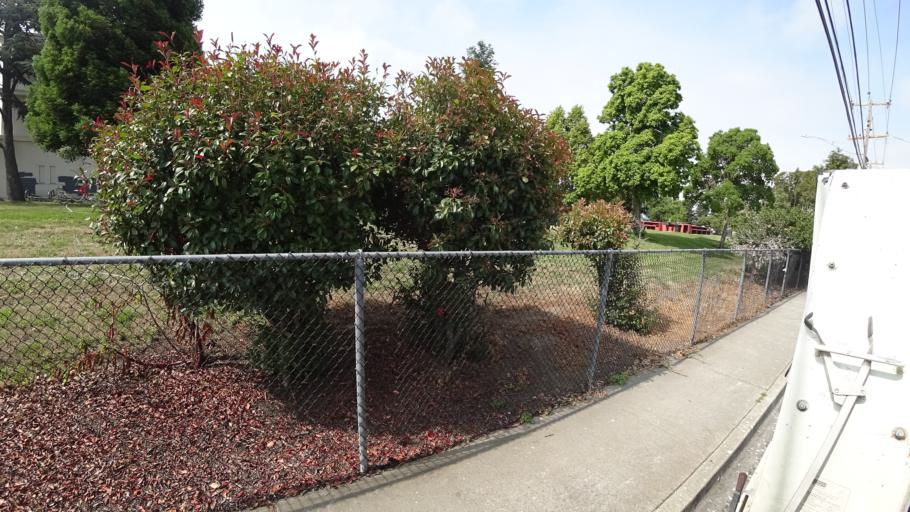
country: US
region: California
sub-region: Alameda County
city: Hayward
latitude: 37.6316
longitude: -122.0989
